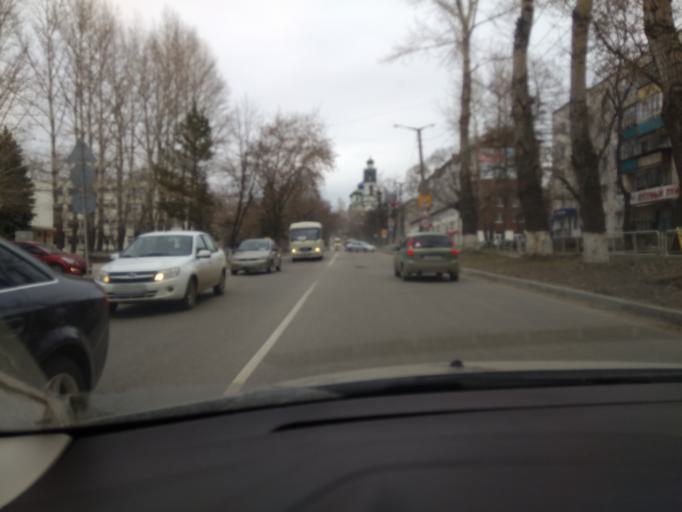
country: RU
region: Chelyabinsk
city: Kyshtym
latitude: 55.7078
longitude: 60.5429
